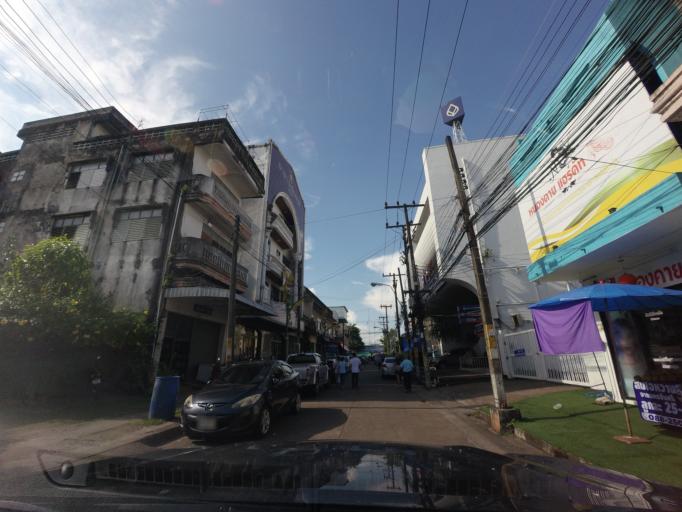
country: TH
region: Nong Khai
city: Nong Khai
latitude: 17.8845
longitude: 102.7477
